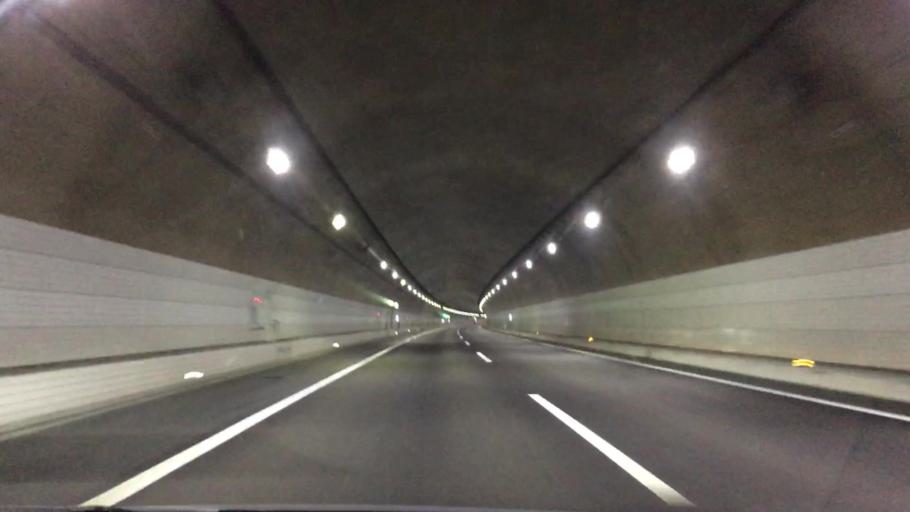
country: JP
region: Aichi
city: Shinshiro
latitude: 34.8361
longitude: 137.5960
